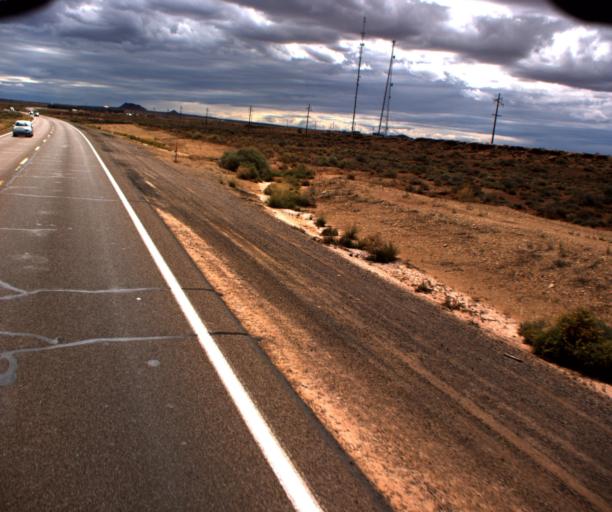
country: US
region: Arizona
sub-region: Navajo County
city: Holbrook
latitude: 34.8795
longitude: -110.1626
